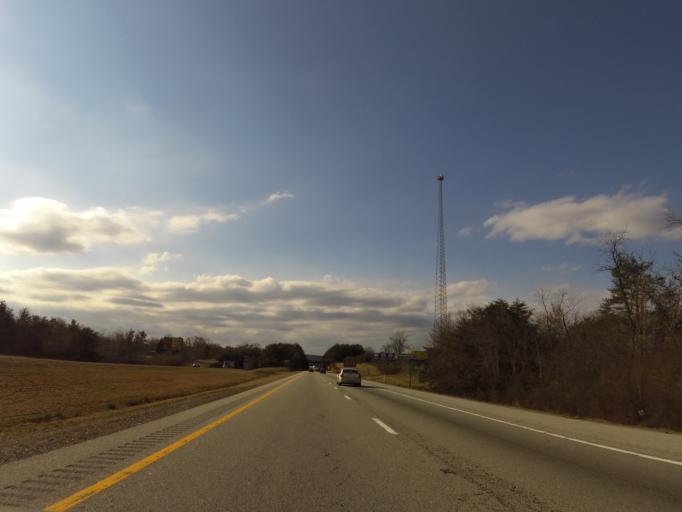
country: US
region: Tennessee
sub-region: Cumberland County
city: Crossville
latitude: 35.9529
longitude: -84.9495
